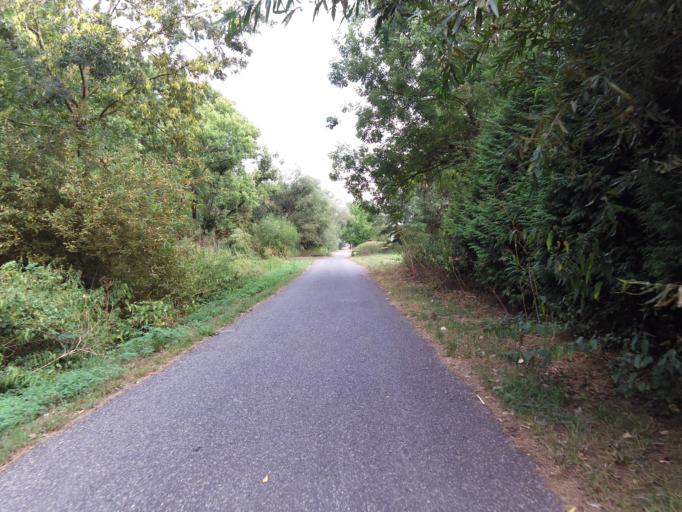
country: DE
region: Bavaria
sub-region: Regierungsbezirk Unterfranken
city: Worth am Main
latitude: 49.8016
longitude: 9.1496
